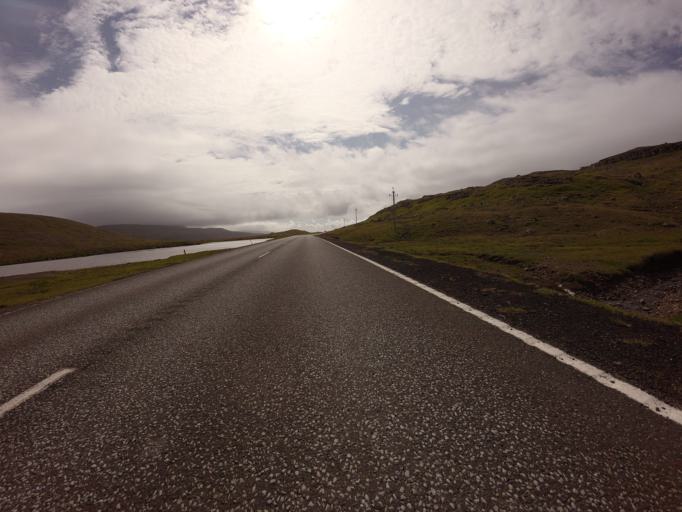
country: FO
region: Sandoy
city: Sandur
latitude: 61.8808
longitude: -6.8651
